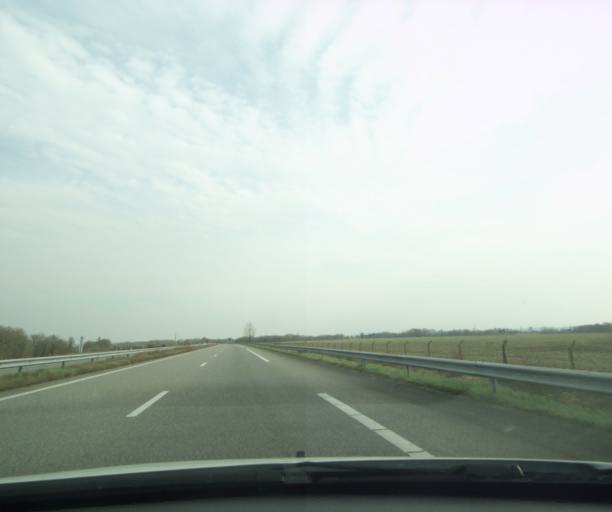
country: FR
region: Aquitaine
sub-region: Departement des Pyrenees-Atlantiques
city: Mont
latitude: 43.4311
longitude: -0.6296
